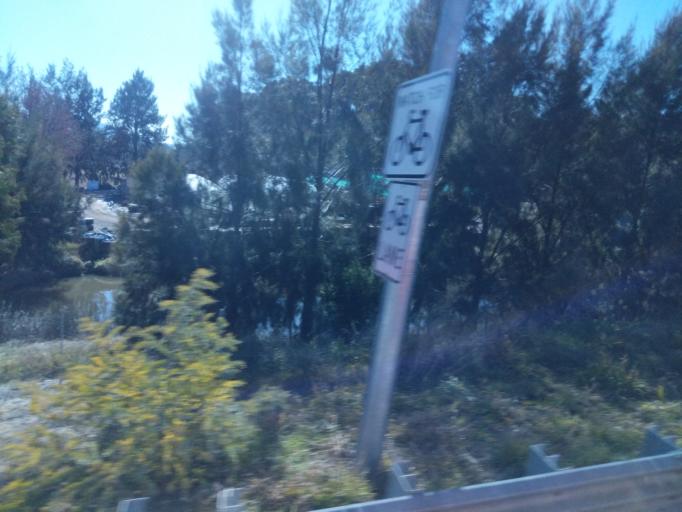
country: AU
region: Australian Capital Territory
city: Forrest
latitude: -35.3025
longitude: 149.1783
